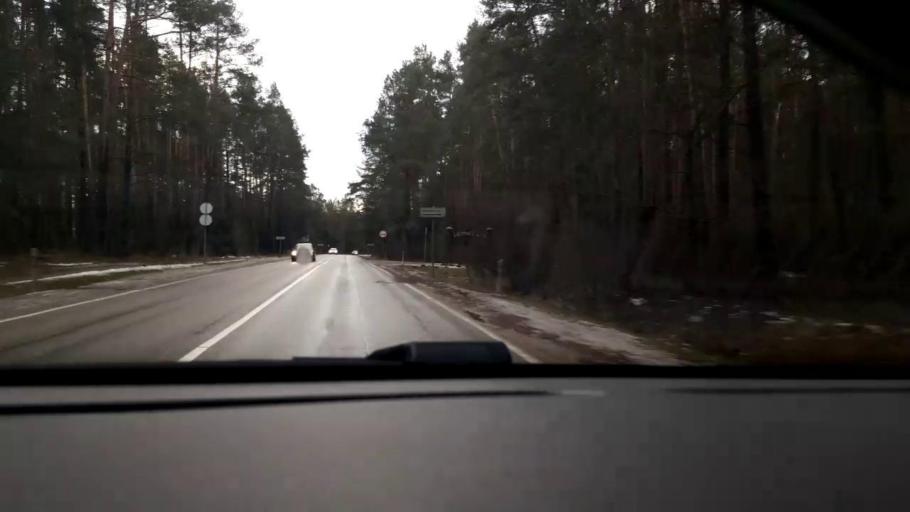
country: LT
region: Vilnius County
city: Rasos
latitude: 54.7767
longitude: 25.3840
